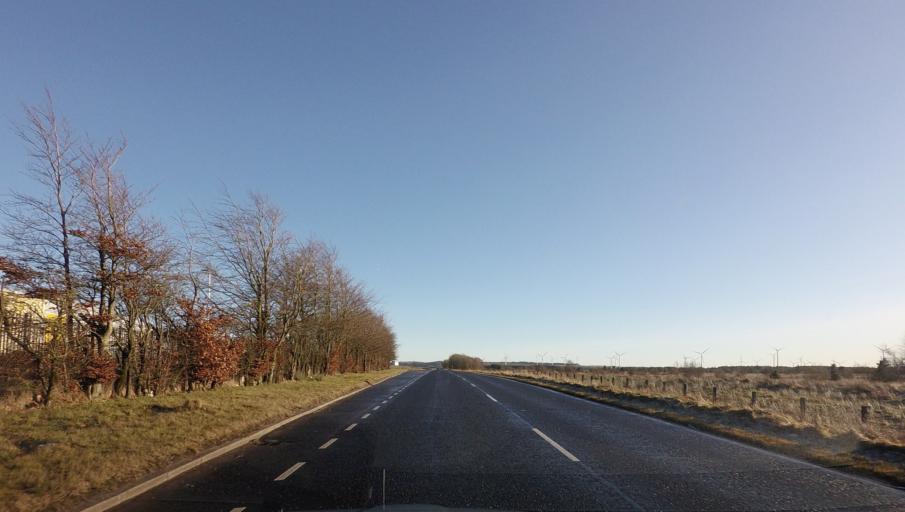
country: GB
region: Scotland
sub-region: North Lanarkshire
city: Shotts
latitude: 55.8061
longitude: -3.7754
